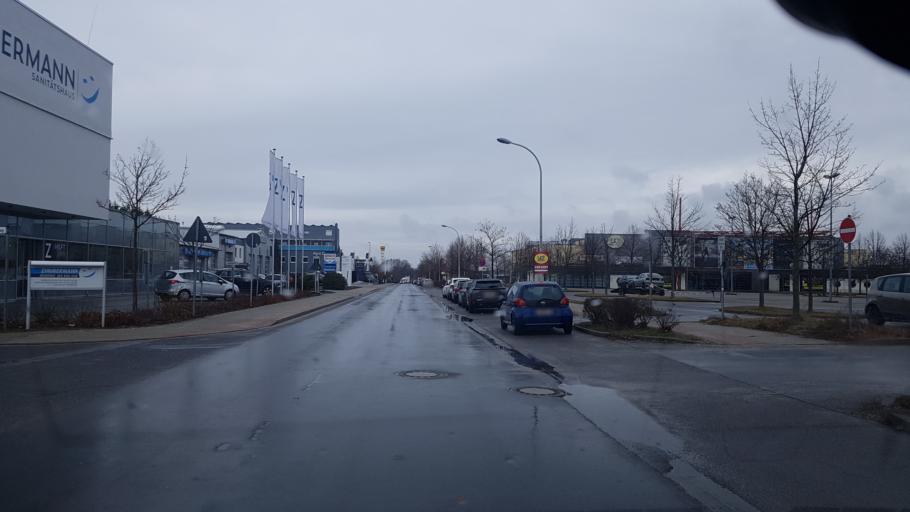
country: DE
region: Brandenburg
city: Cottbus
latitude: 51.7179
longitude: 14.3154
